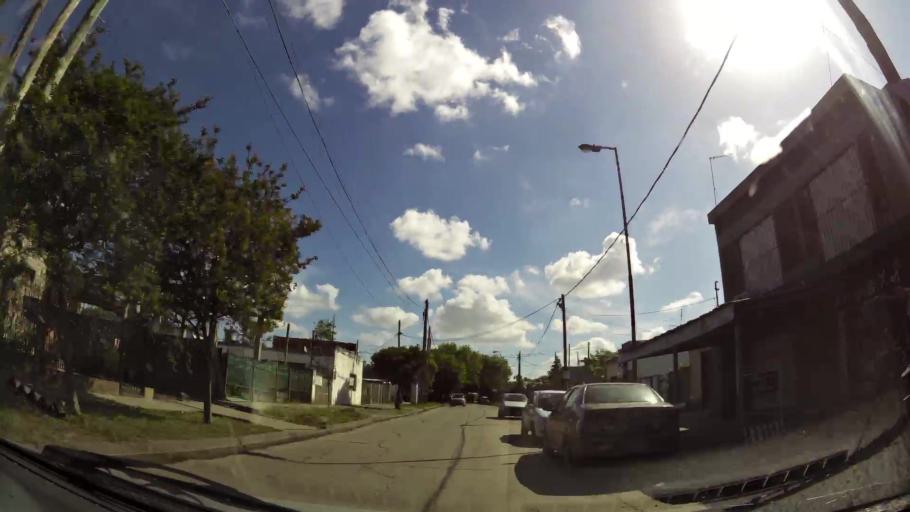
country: AR
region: Buenos Aires
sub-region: Partido de Quilmes
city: Quilmes
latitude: -34.8017
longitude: -58.2560
